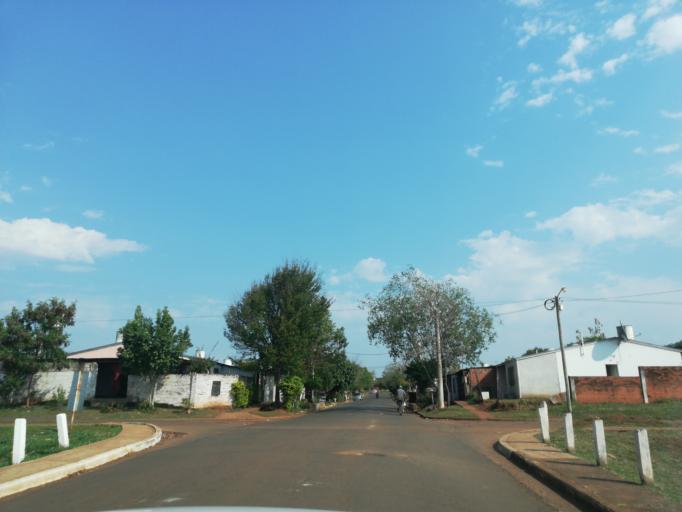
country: AR
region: Misiones
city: Garupa
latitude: -27.4322
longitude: -55.8753
